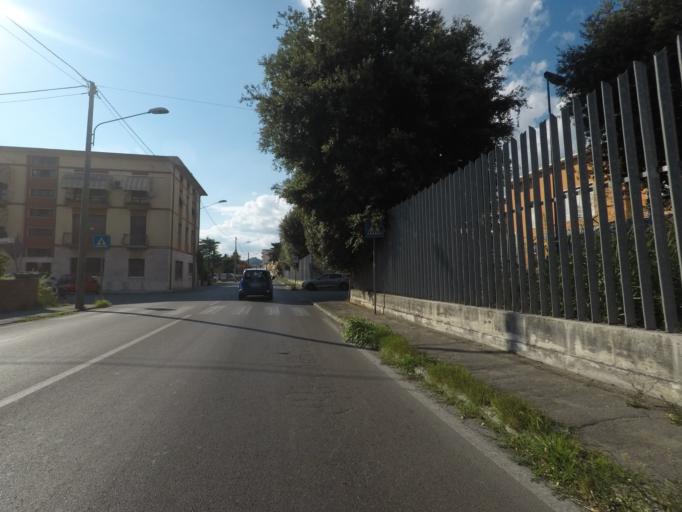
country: IT
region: Tuscany
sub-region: Provincia di Massa-Carrara
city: Massa
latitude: 44.0228
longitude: 10.1392
